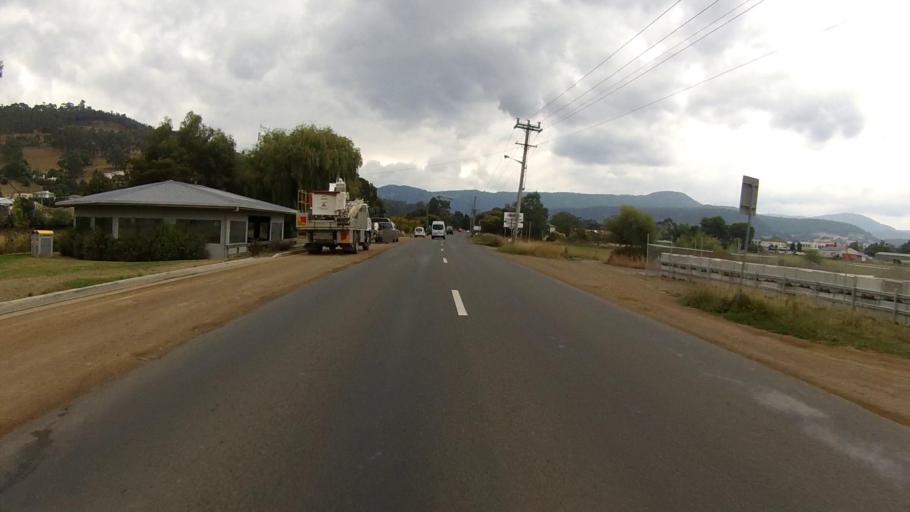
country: AU
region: Tasmania
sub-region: Huon Valley
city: Huonville
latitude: -43.0349
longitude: 147.0503
